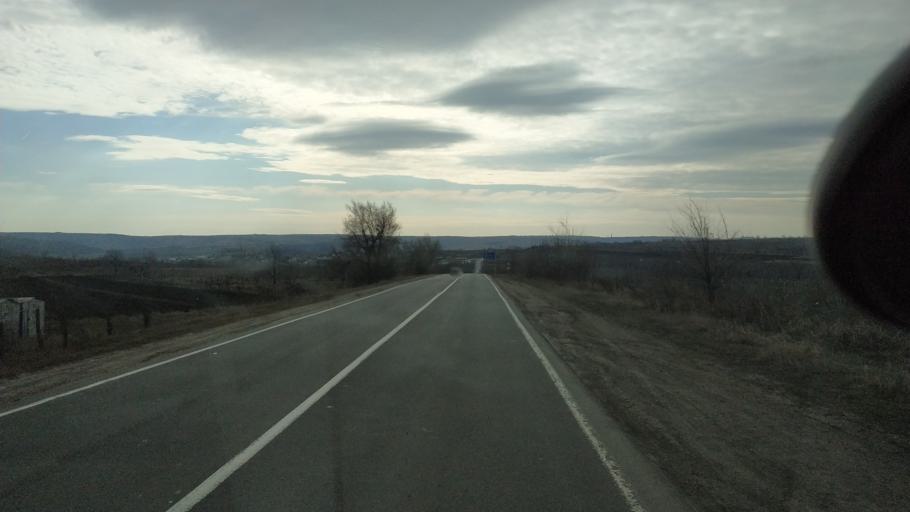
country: MD
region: Chisinau
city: Vadul lui Voda
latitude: 47.0764
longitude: 29.0266
